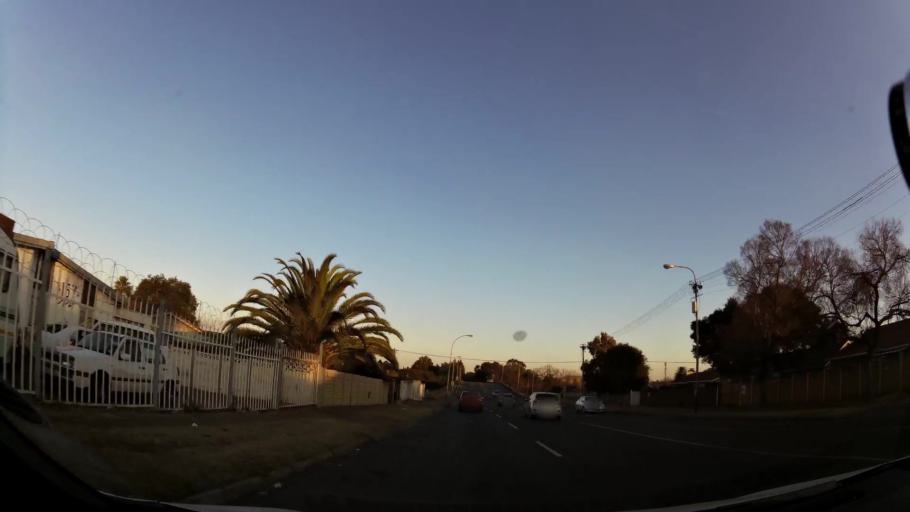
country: ZA
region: Gauteng
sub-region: Ekurhuleni Metropolitan Municipality
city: Germiston
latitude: -26.2666
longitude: 28.1646
